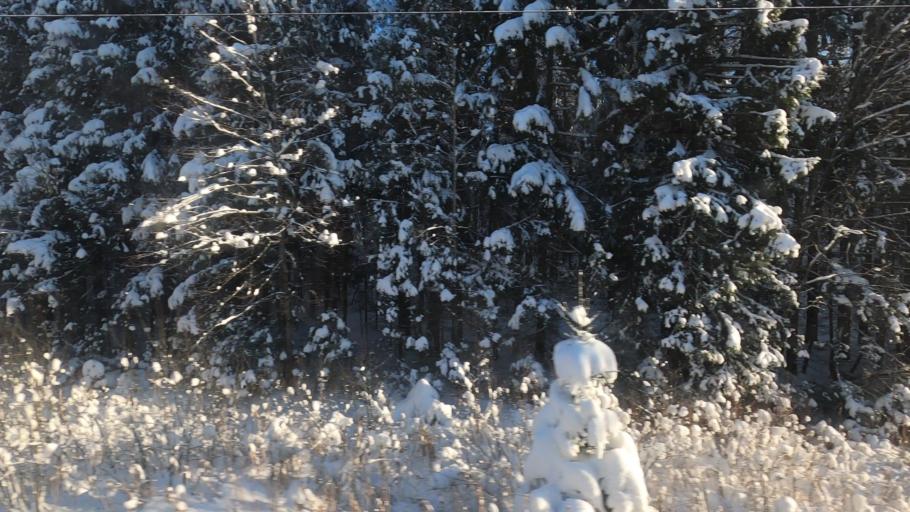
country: RU
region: Moskovskaya
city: Zhukovka
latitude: 56.5064
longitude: 37.5542
